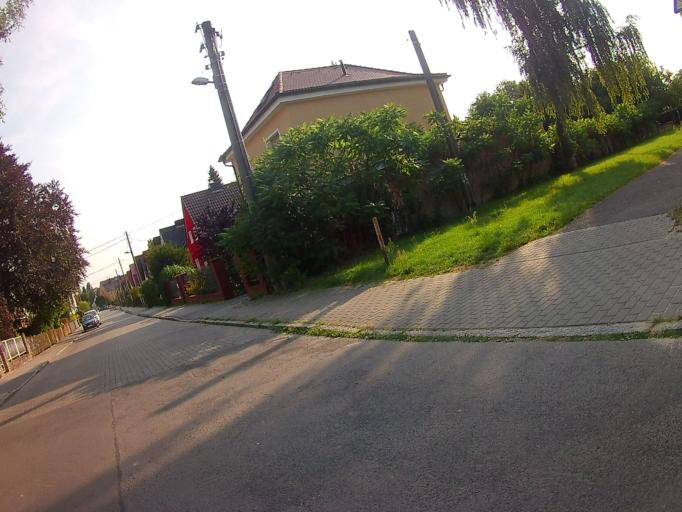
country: DE
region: Berlin
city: Biesdorf
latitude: 52.5175
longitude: 13.5597
